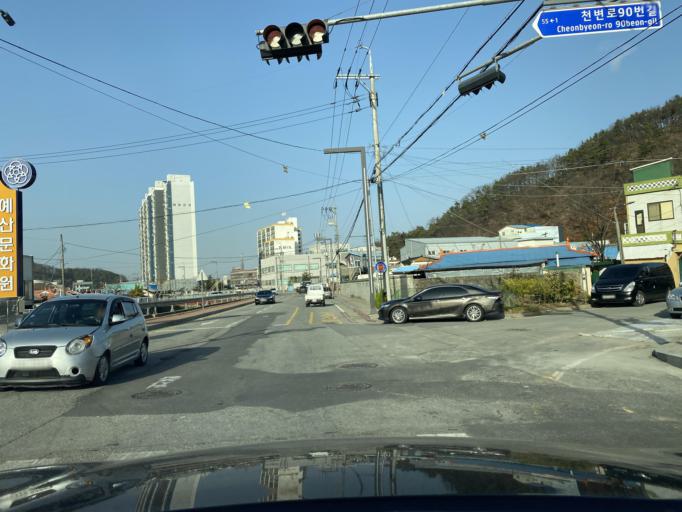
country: KR
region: Chungcheongnam-do
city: Yesan
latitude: 36.6775
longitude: 126.8405
